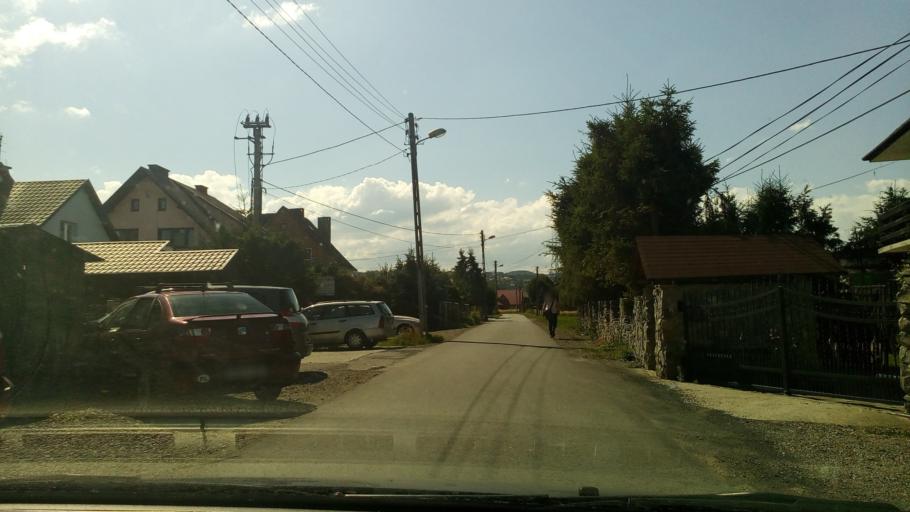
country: PL
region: Lesser Poland Voivodeship
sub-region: Powiat nowosadecki
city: Chelmiec
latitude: 49.6274
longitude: 20.6636
